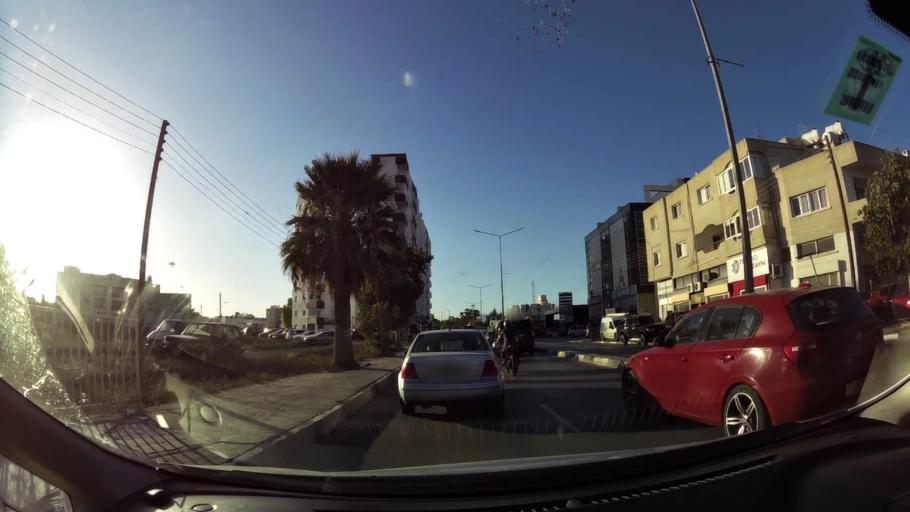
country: CY
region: Lefkosia
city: Nicosia
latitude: 35.2034
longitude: 33.3334
